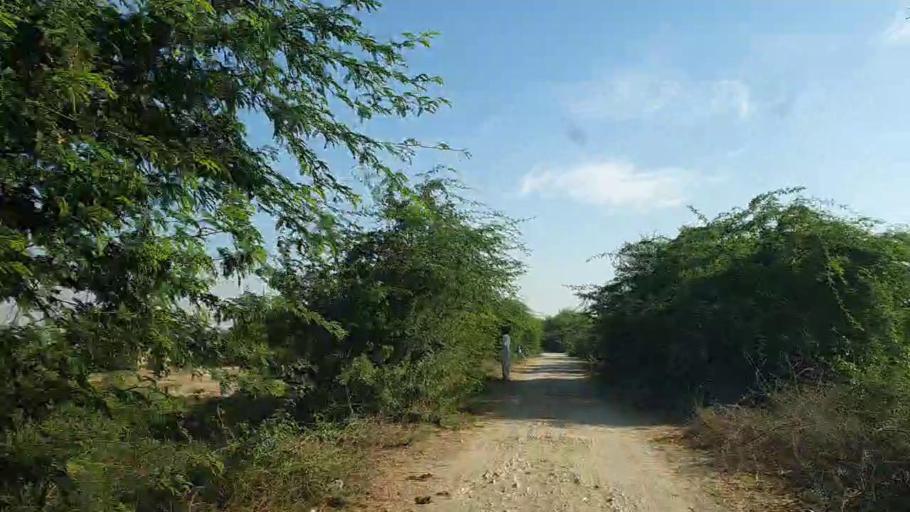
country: PK
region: Sindh
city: Bulri
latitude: 24.7865
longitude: 68.3492
